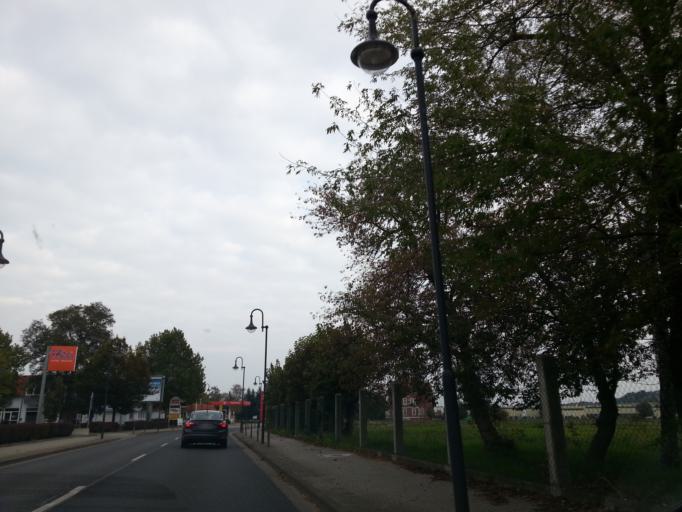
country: DE
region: Saxony
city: Radebeul
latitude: 51.0871
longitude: 13.6380
